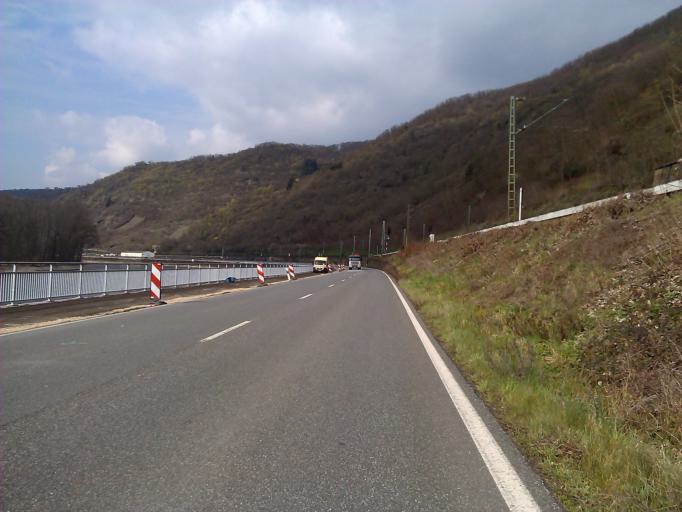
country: DE
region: Rheinland-Pfalz
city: Bacharach
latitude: 50.0714
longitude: 7.7780
